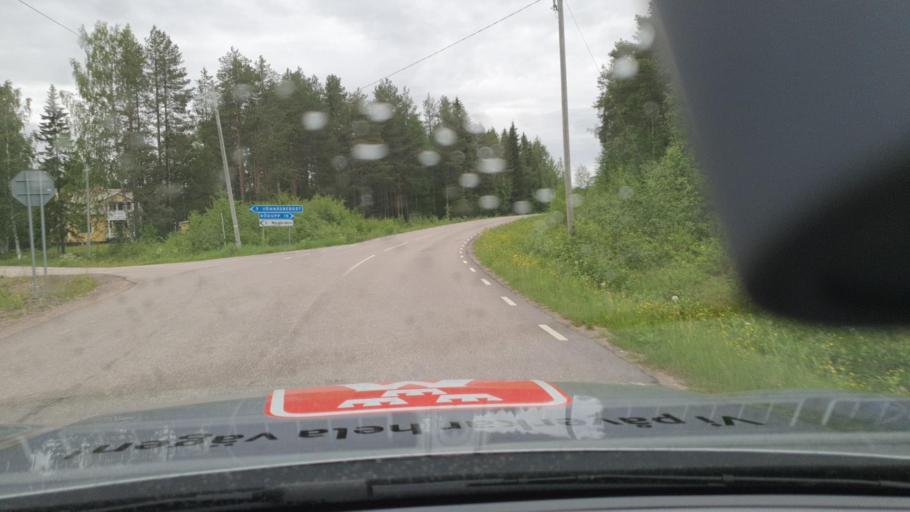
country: SE
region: Norrbotten
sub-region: Overkalix Kommun
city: OEverkalix
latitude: 66.3530
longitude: 22.7990
